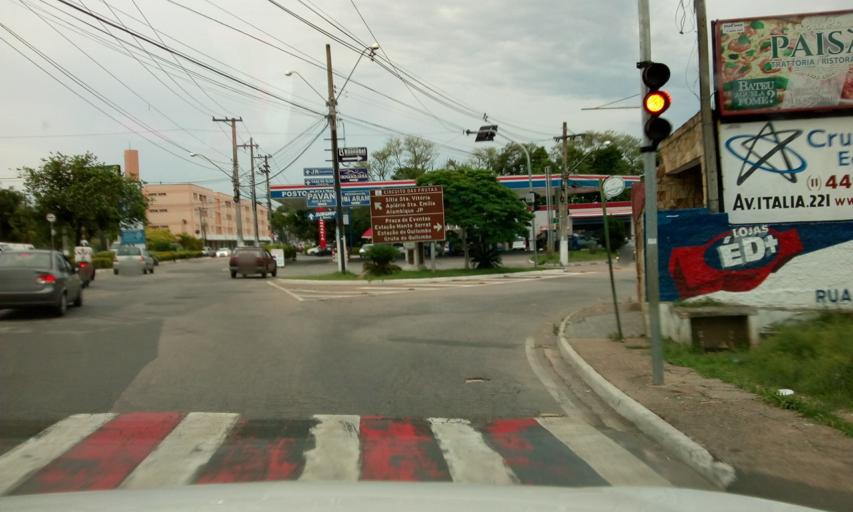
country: BR
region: Sao Paulo
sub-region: Itupeva
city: Itupeva
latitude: -23.1549
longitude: -47.0522
